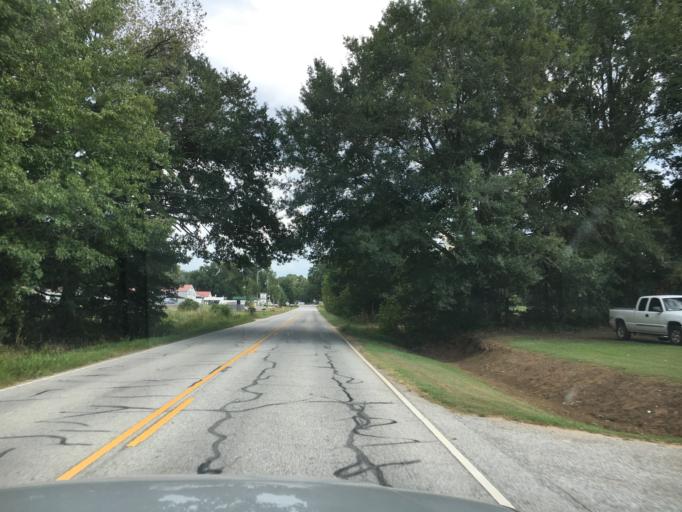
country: US
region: South Carolina
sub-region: Greenwood County
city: Ninety Six
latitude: 34.1878
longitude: -82.0284
